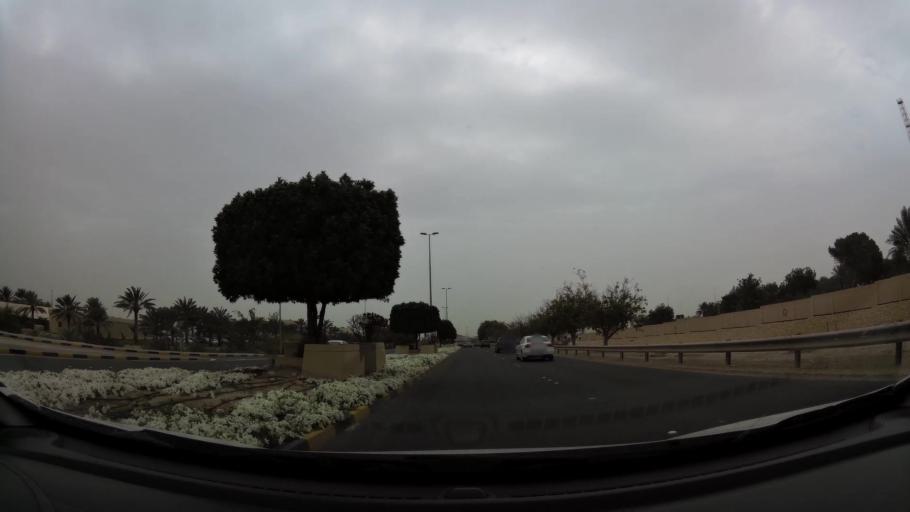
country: BH
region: Northern
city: Ar Rifa'
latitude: 26.1438
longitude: 50.5432
